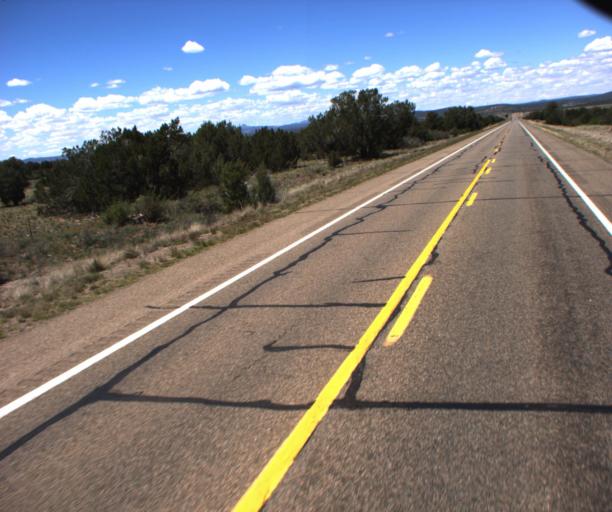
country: US
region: Arizona
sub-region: Coconino County
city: Williams
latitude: 35.1761
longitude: -112.4632
